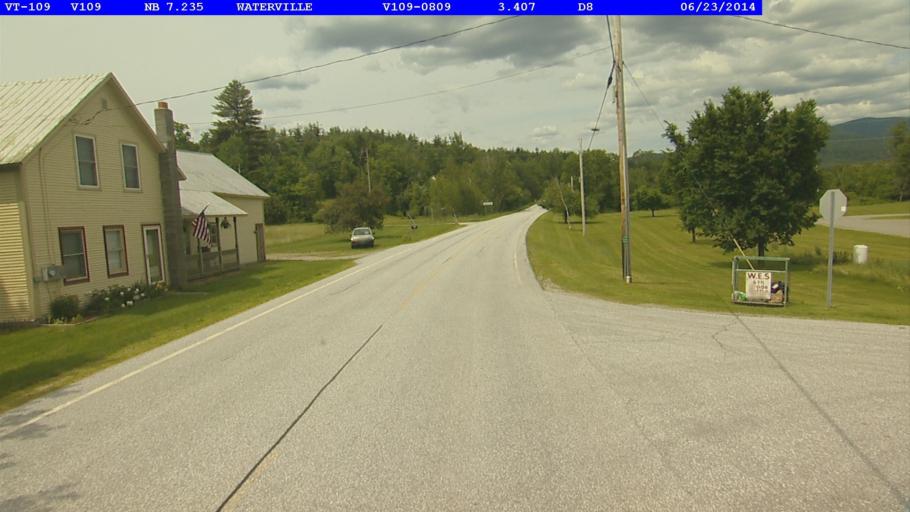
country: US
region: Vermont
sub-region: Lamoille County
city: Johnson
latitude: 44.7266
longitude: -72.7495
